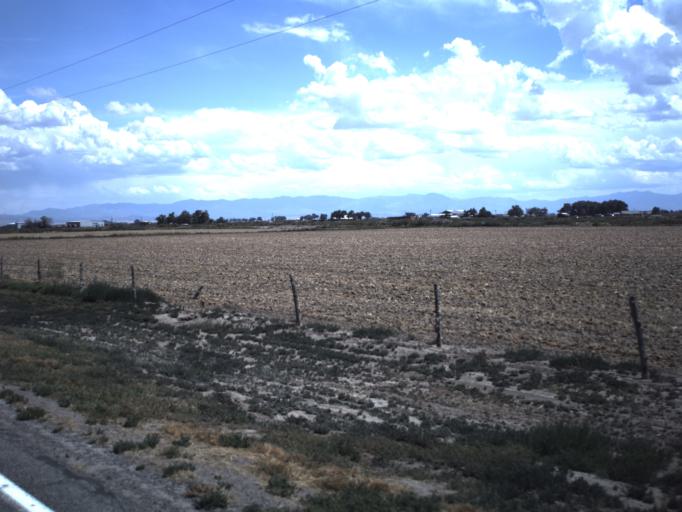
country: US
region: Utah
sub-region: Millard County
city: Delta
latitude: 39.3307
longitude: -112.6614
